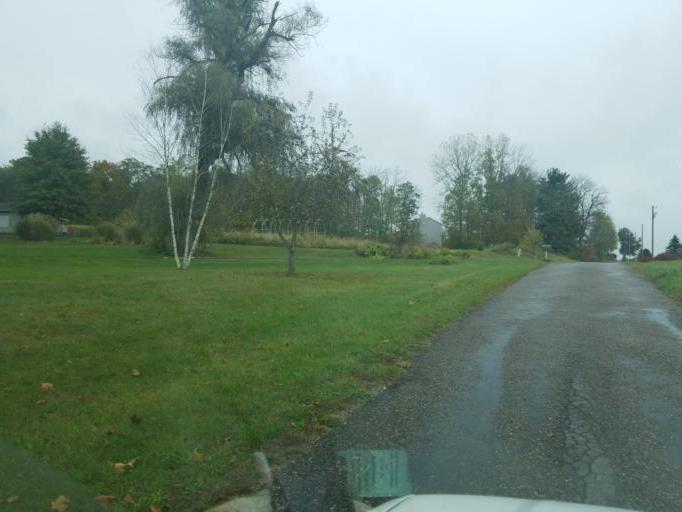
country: US
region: Ohio
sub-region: Wayne County
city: Shreve
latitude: 40.5964
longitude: -82.0331
